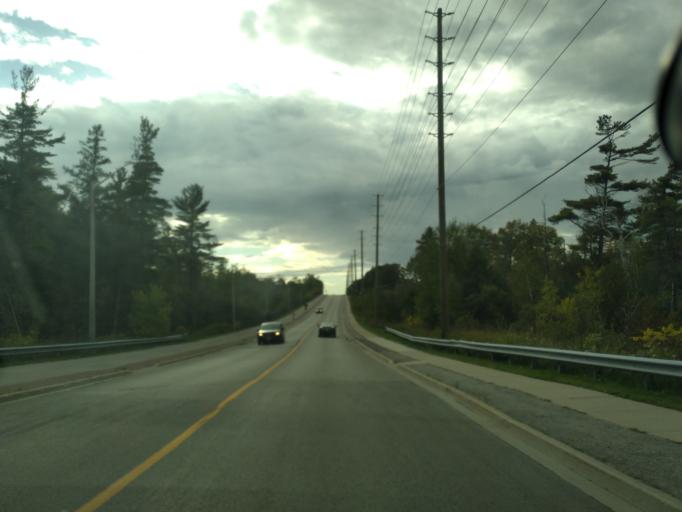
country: CA
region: Ontario
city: Newmarket
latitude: 43.9857
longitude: -79.4436
